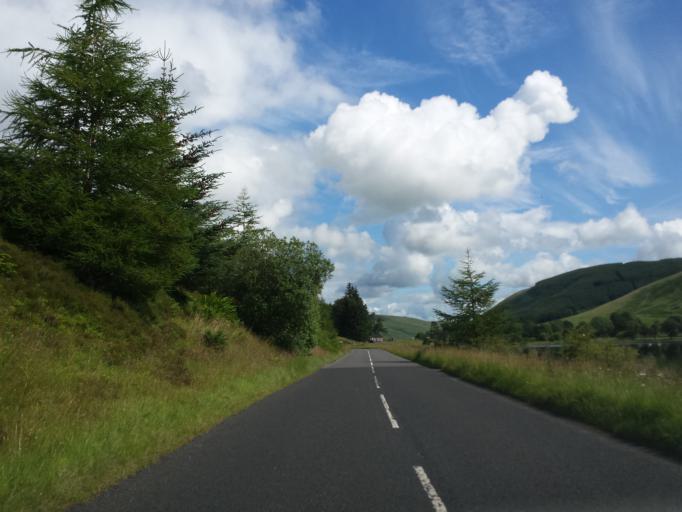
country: GB
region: Scotland
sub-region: The Scottish Borders
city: Peebles
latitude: 55.4683
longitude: -3.2093
